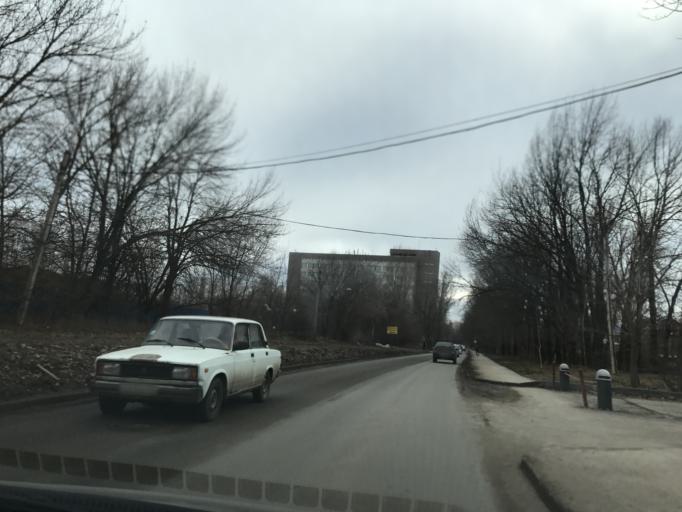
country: RU
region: Rostov
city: Rostov-na-Donu
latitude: 47.2214
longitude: 39.6266
